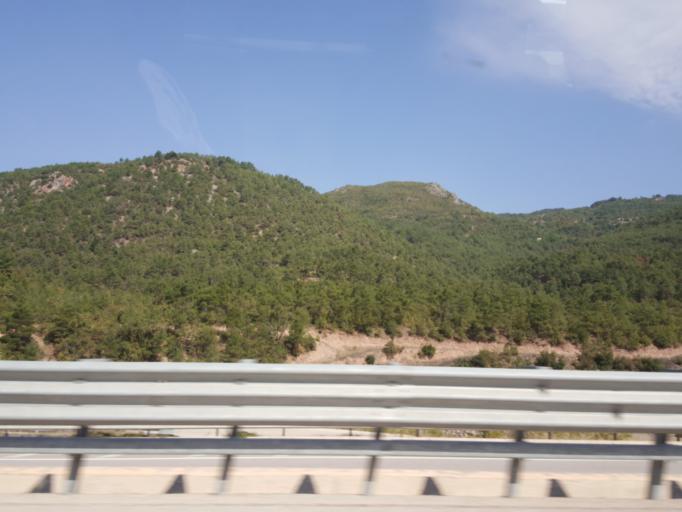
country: TR
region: Tokat
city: Basciftlik
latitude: 40.4576
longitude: 37.0468
